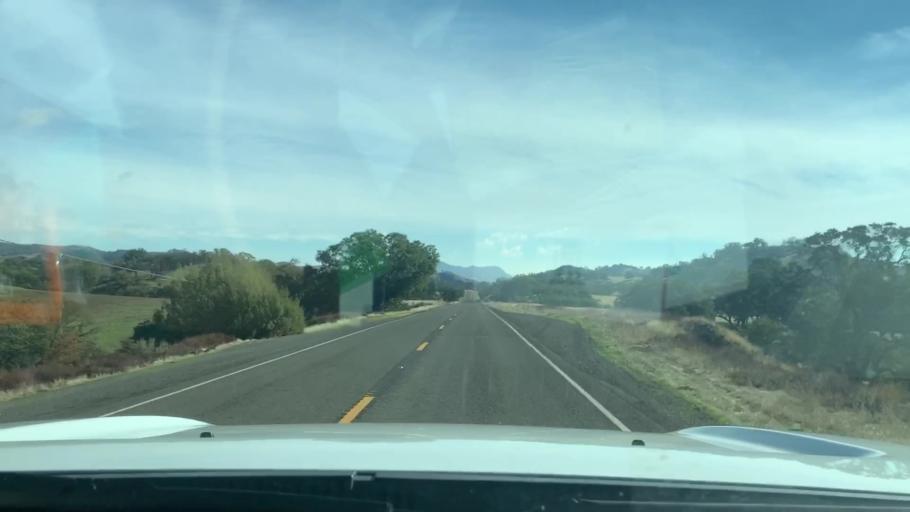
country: US
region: California
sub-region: Fresno County
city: Coalinga
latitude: 36.0990
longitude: -120.5355
